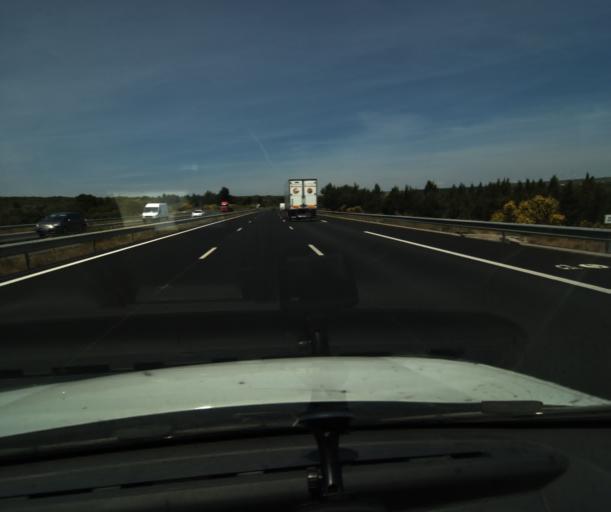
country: FR
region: Languedoc-Roussillon
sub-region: Departement de l'Aude
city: Sigean
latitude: 42.9635
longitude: 2.9690
